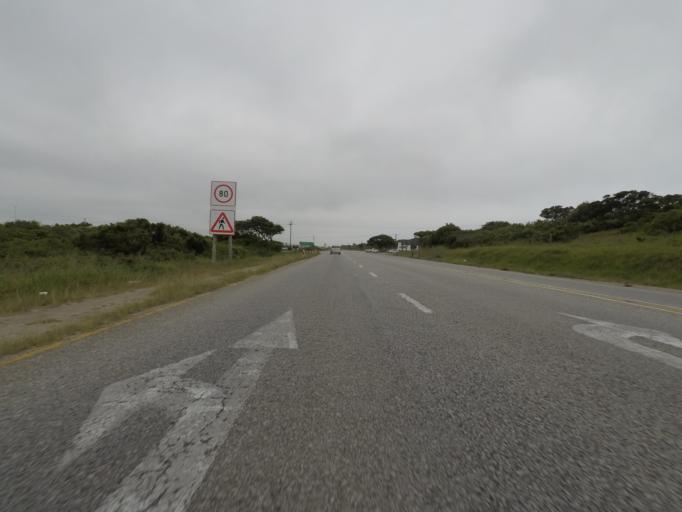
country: ZA
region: Eastern Cape
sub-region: Cacadu District Municipality
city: Port Alfred
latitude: -33.6794
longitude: 26.6658
